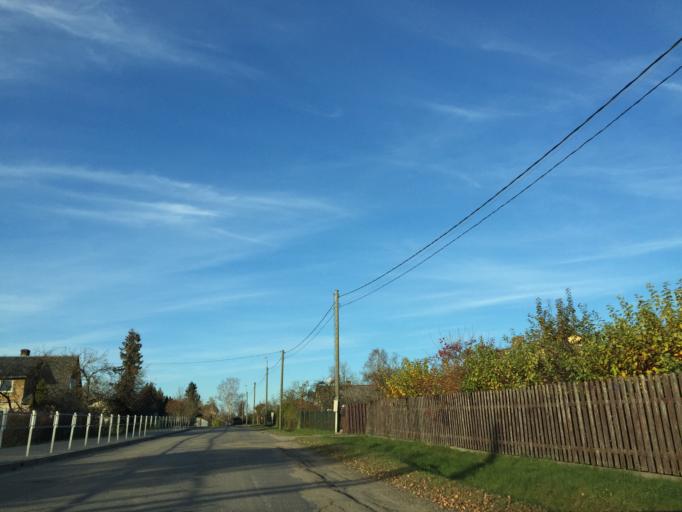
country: LV
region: Skriveri
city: Skriveri
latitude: 56.6350
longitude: 25.1180
